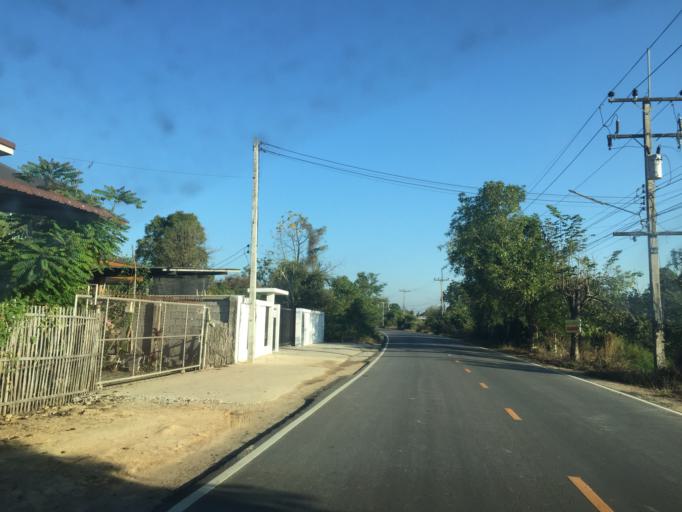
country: TH
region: Lamphun
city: Ban Thi
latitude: 18.6186
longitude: 99.0572
